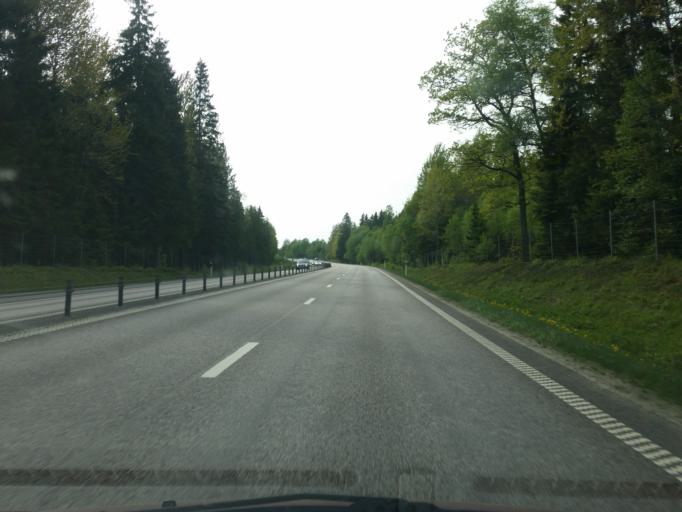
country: SE
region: Vaestra Goetaland
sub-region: Ulricehamns Kommun
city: Ulricehamn
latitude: 57.7991
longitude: 13.5269
